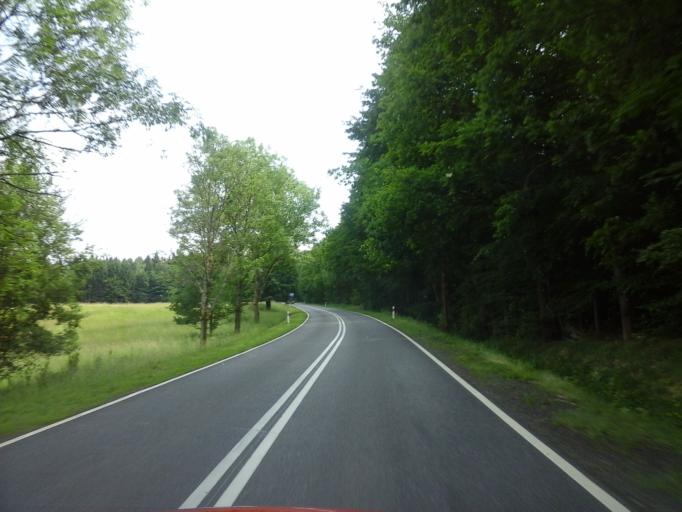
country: PL
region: West Pomeranian Voivodeship
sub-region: Powiat stargardzki
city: Insko
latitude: 53.4848
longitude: 15.5800
